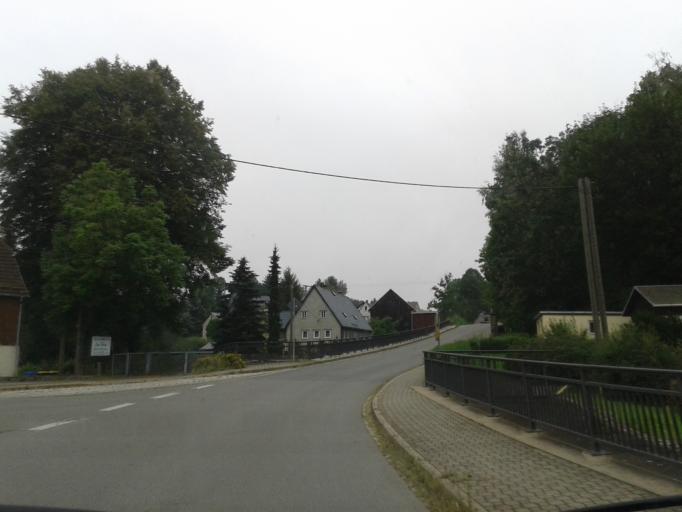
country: DE
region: Saxony
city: Grossschirma
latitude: 50.9662
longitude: 13.3113
